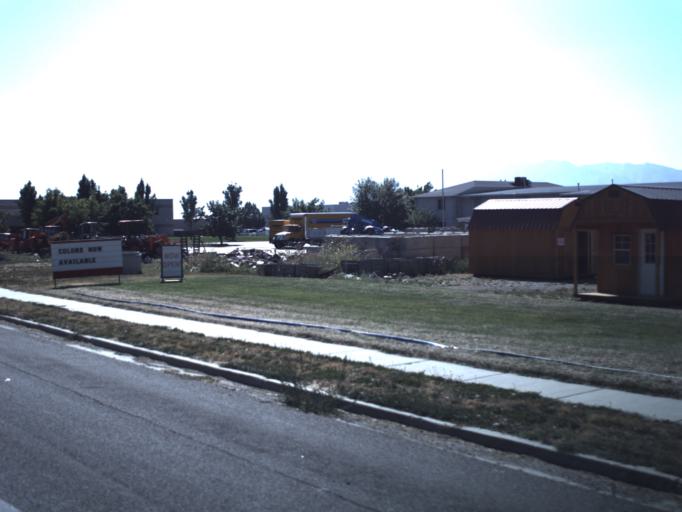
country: US
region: Utah
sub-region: Cache County
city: Hyde Park
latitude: 41.8028
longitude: -111.8335
